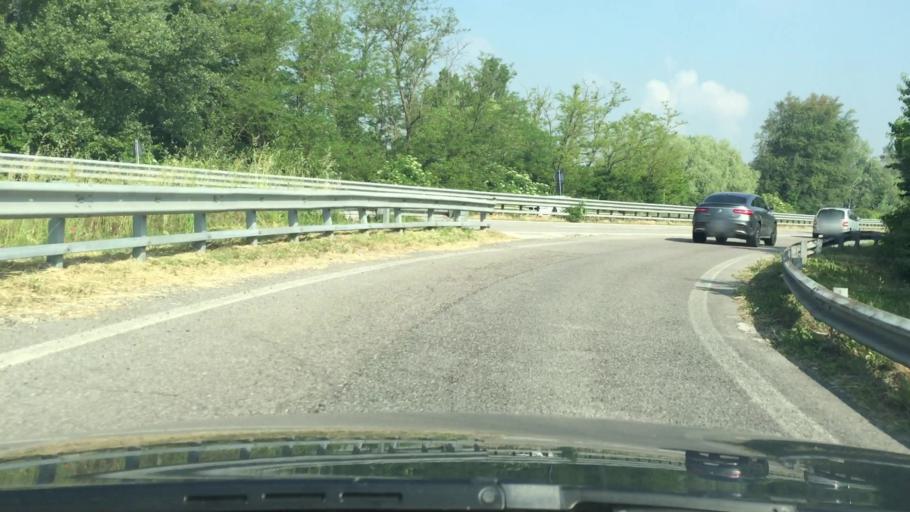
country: IT
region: Emilia-Romagna
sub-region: Provincia di Ferrara
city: Gaibanella-Sant'Edigio
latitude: 44.7965
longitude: 11.6373
